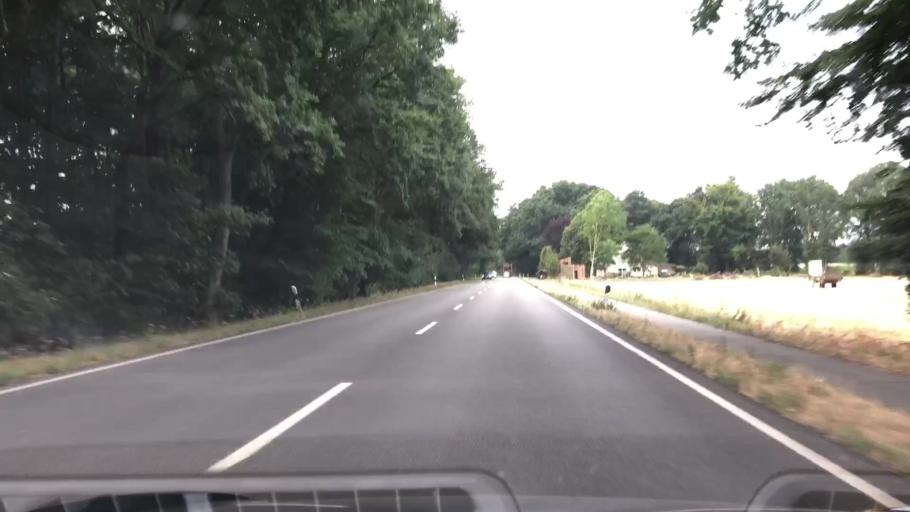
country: DE
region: Lower Saxony
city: Cloppenburg
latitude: 52.8724
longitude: 8.0870
